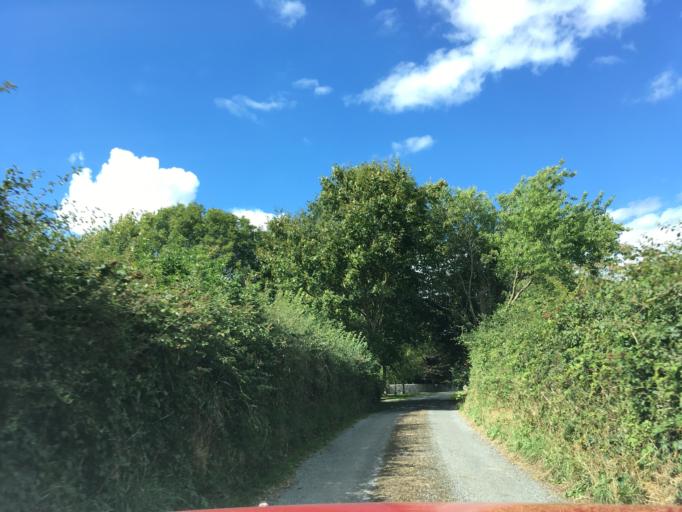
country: IE
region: Munster
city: Cashel
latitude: 52.4614
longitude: -7.9418
